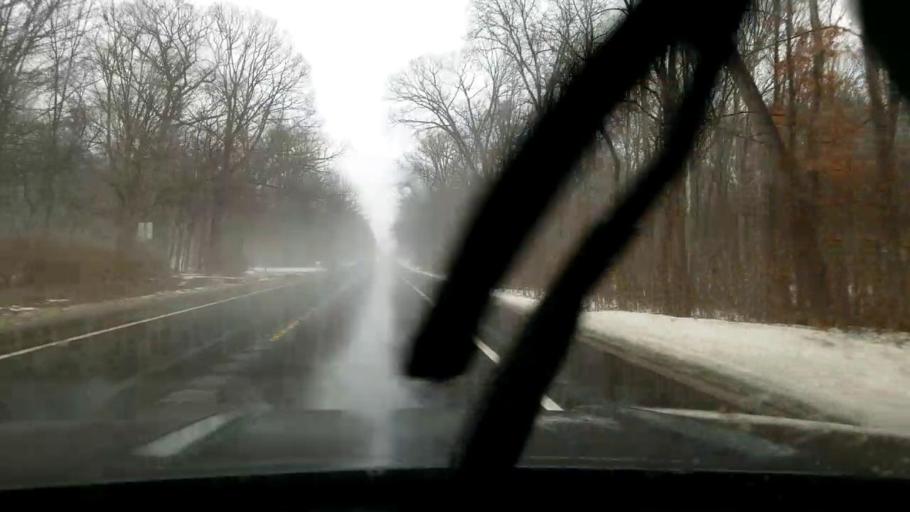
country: US
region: Michigan
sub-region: Jackson County
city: Napoleon
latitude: 42.1782
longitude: -84.2858
